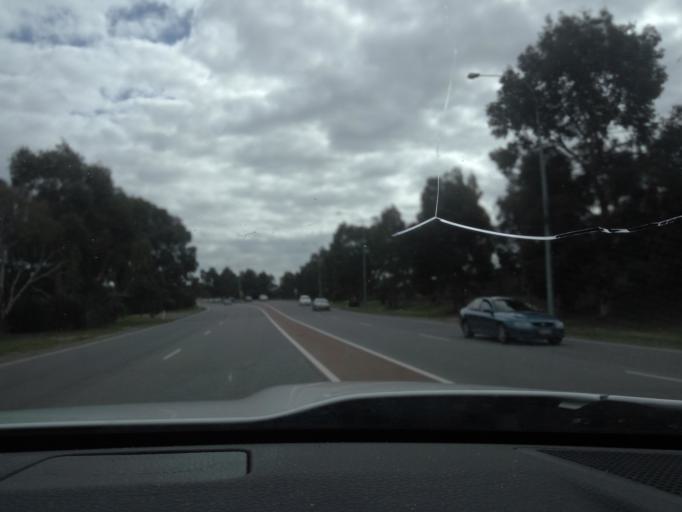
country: AU
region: Western Australia
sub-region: City of Cockburn
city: Bibra Lake
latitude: -32.1050
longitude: 115.8252
